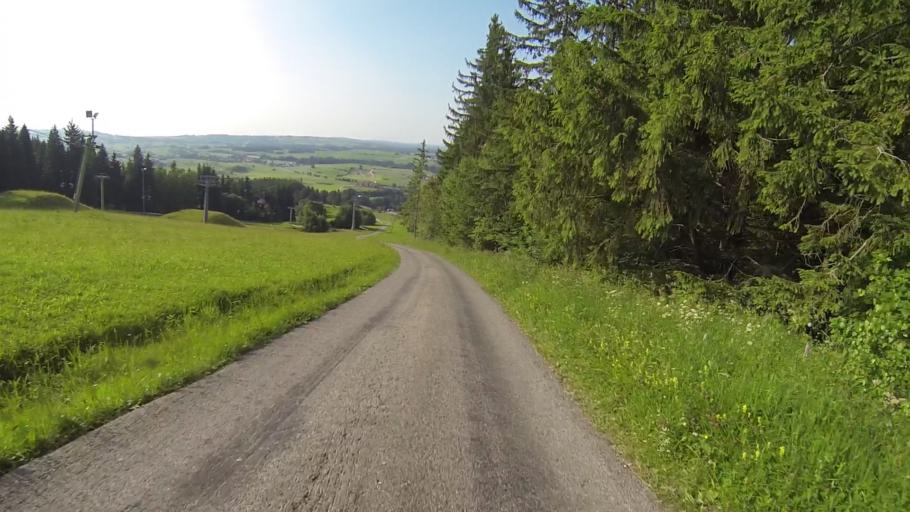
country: DE
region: Bavaria
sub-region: Swabia
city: Nesselwang
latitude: 47.6114
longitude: 10.4980
